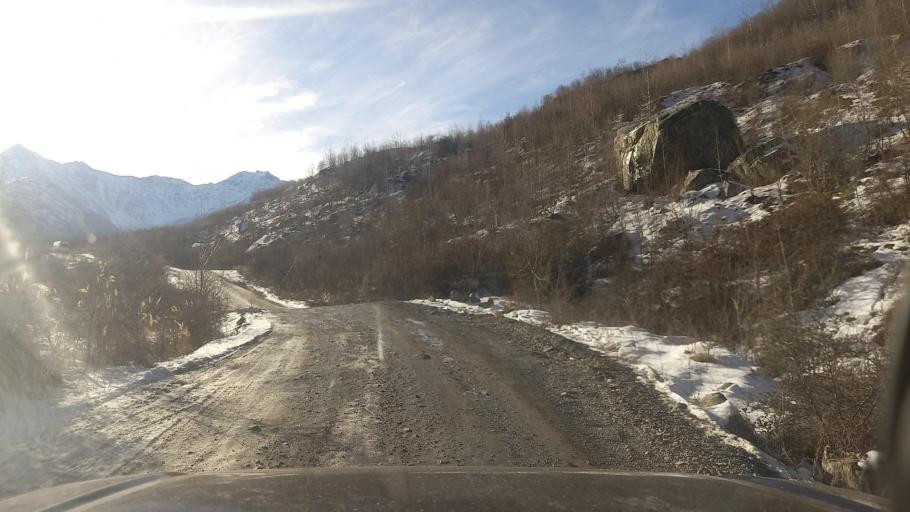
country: RU
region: Ingushetiya
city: Dzhayrakh
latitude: 42.8607
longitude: 44.5197
